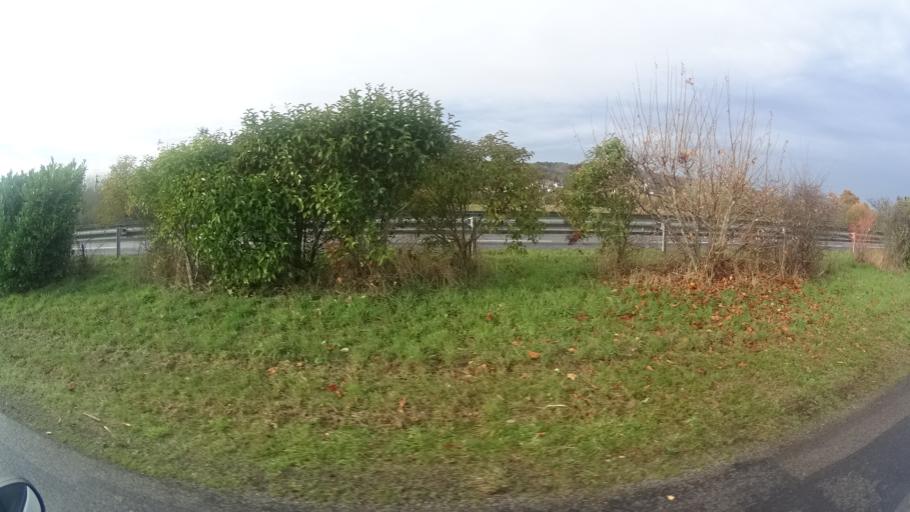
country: FR
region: Brittany
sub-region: Departement du Morbihan
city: Rieux
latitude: 47.6223
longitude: -2.1014
